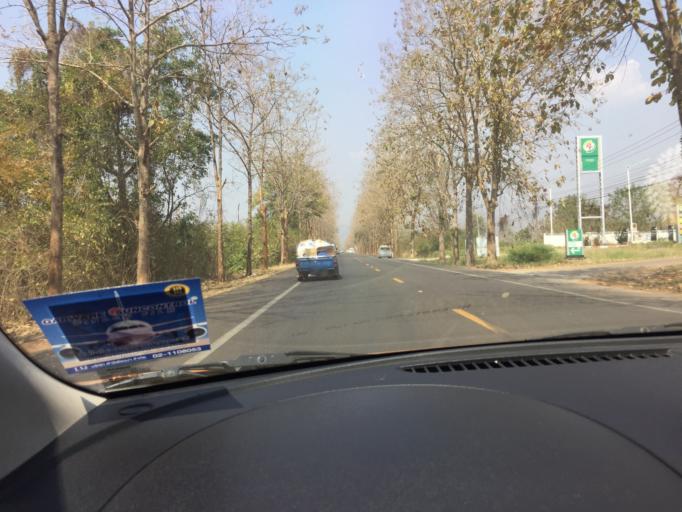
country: TH
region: Kanchanaburi
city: Sai Yok
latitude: 14.1784
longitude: 99.1266
